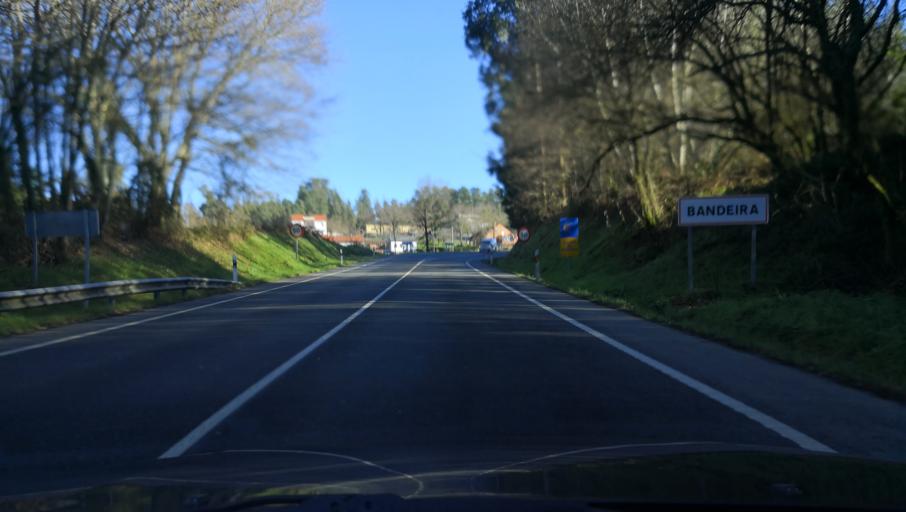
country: ES
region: Galicia
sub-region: Provincia de Pontevedra
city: Silleda
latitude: 42.7306
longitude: -8.3100
